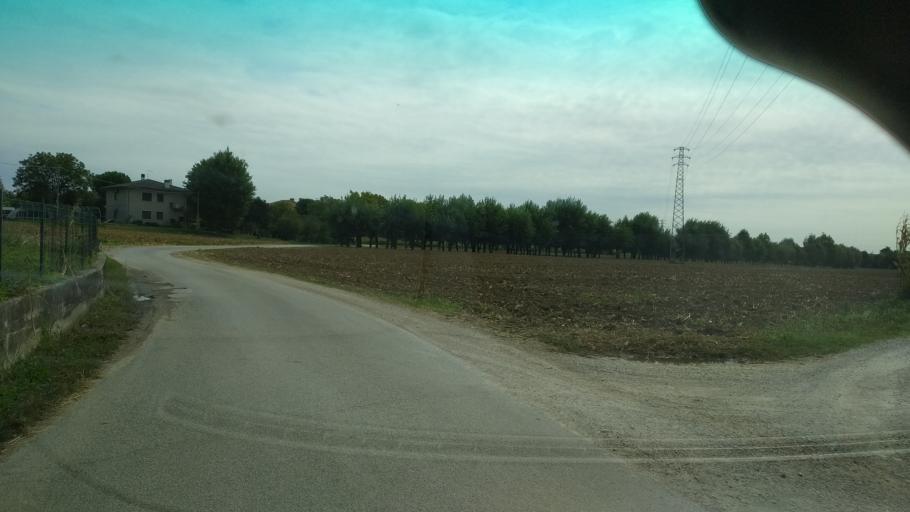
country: IT
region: Veneto
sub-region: Provincia di Vicenza
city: Sandrigo
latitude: 45.6403
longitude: 11.5930
